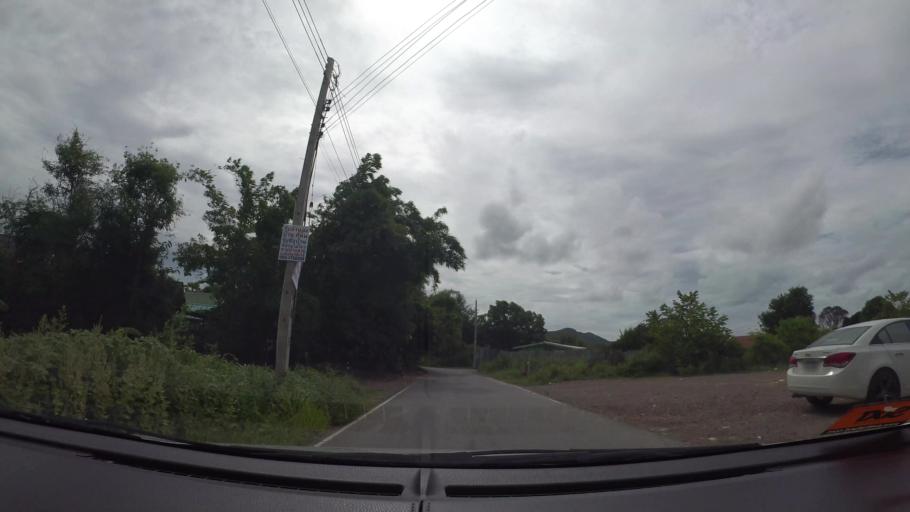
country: TH
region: Chon Buri
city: Sattahip
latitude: 12.7080
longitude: 100.8988
